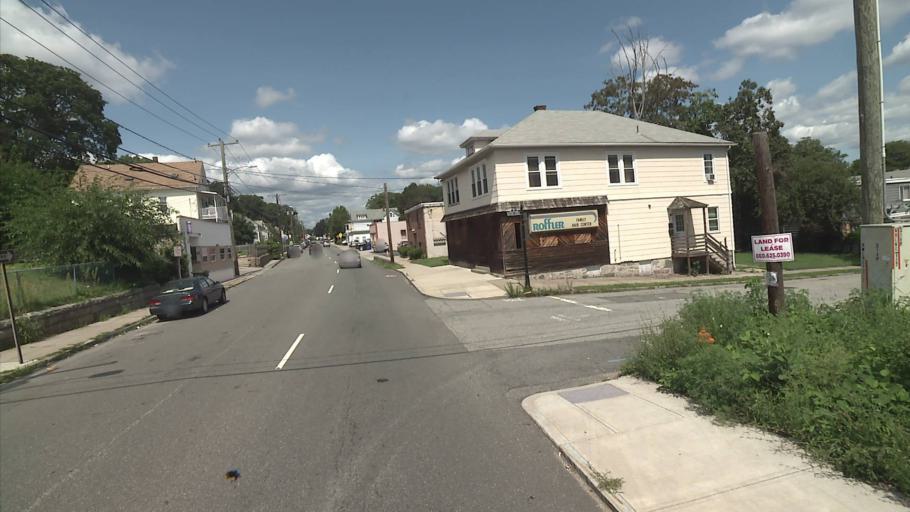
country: US
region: Connecticut
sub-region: New London County
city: New London
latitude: 41.3540
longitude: -72.1104
